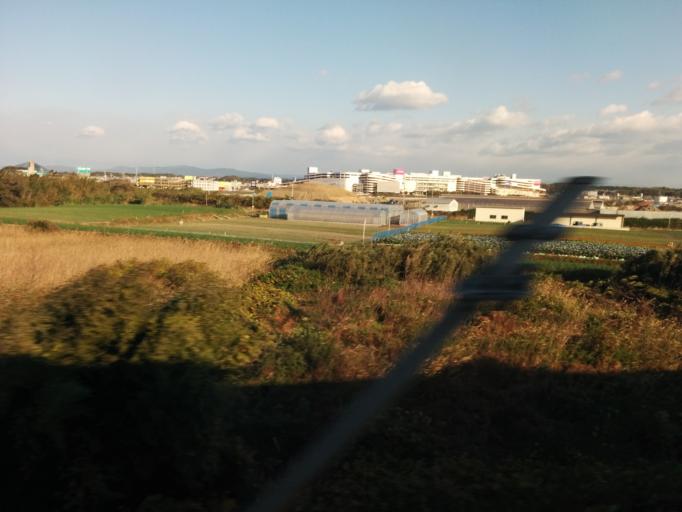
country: JP
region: Shizuoka
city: Hamamatsu
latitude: 34.6883
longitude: 137.6500
